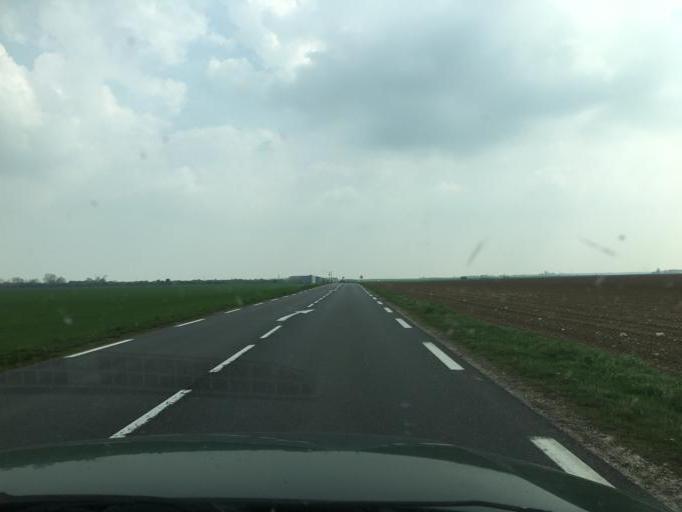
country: FR
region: Centre
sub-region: Departement du Loiret
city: Bricy
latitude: 47.9911
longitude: 1.7253
